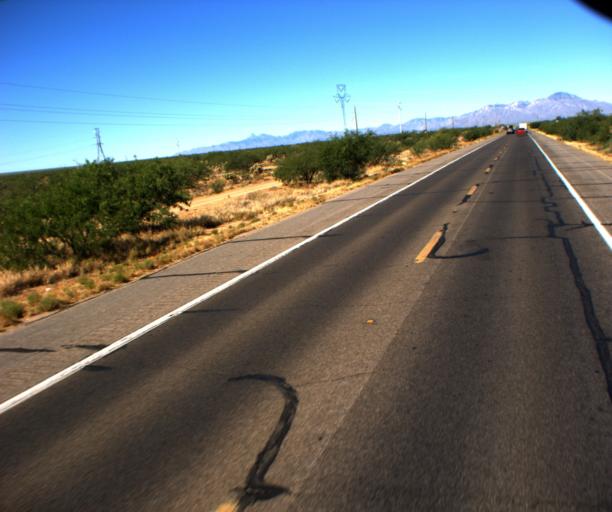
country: US
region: Arizona
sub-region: Pima County
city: Three Points
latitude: 32.0920
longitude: -111.2750
